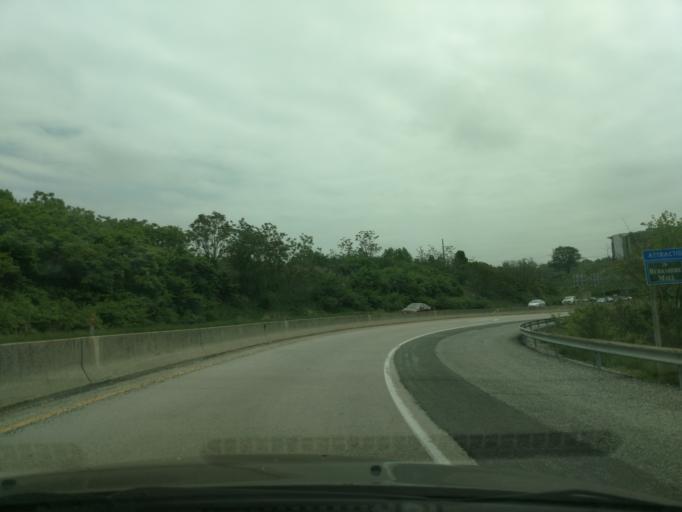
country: US
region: Pennsylvania
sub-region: Berks County
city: Wyomissing
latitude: 40.3381
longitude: -75.9655
